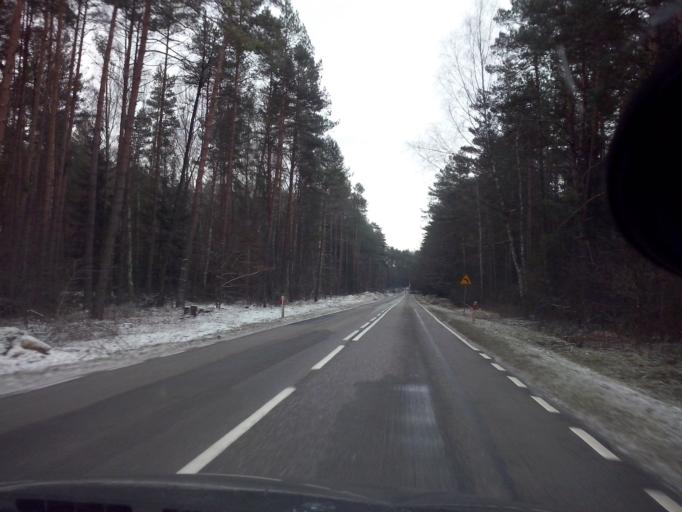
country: PL
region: Lublin Voivodeship
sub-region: Powiat bilgorajski
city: Tereszpol
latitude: 50.5923
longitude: 22.8532
